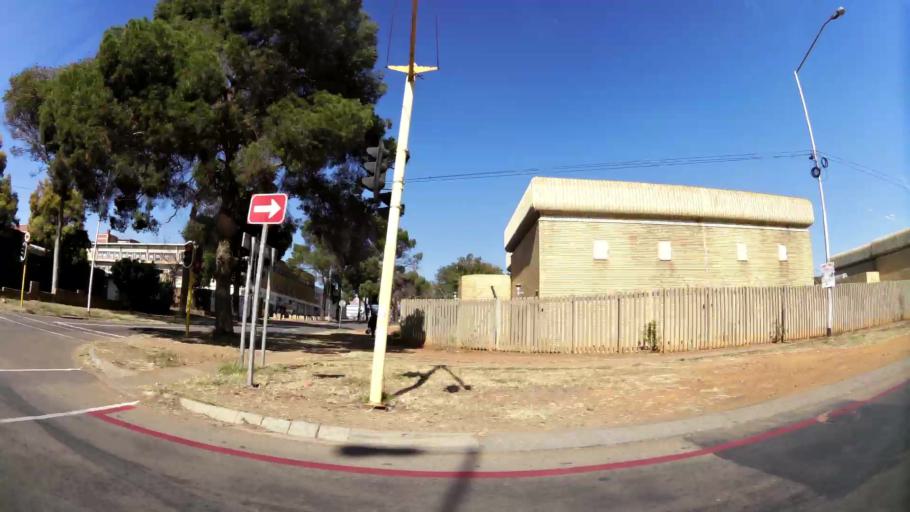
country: ZA
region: Gauteng
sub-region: City of Tshwane Metropolitan Municipality
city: Pretoria
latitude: -25.7516
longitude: 28.1785
